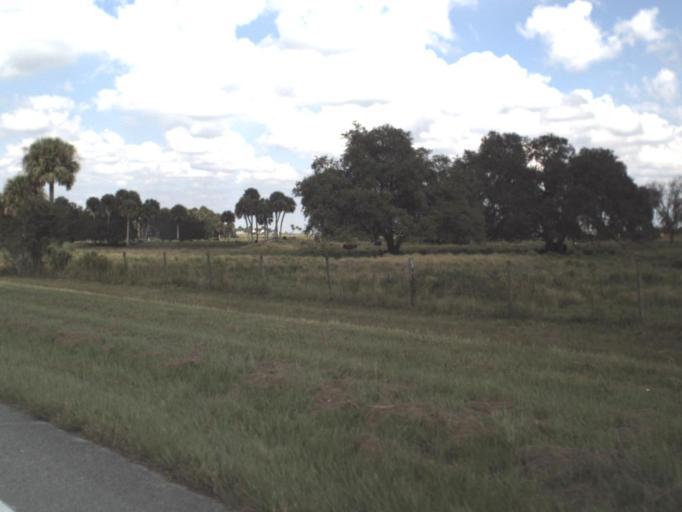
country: US
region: Florida
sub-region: Okeechobee County
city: Okeechobee
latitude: 27.3215
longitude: -80.9171
